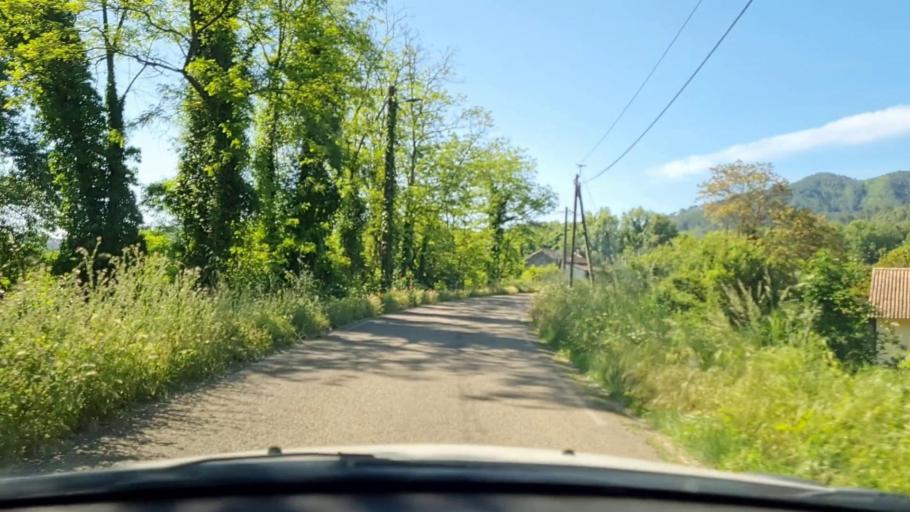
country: FR
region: Languedoc-Roussillon
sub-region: Departement du Gard
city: Cendras
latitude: 44.1573
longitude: 4.0387
